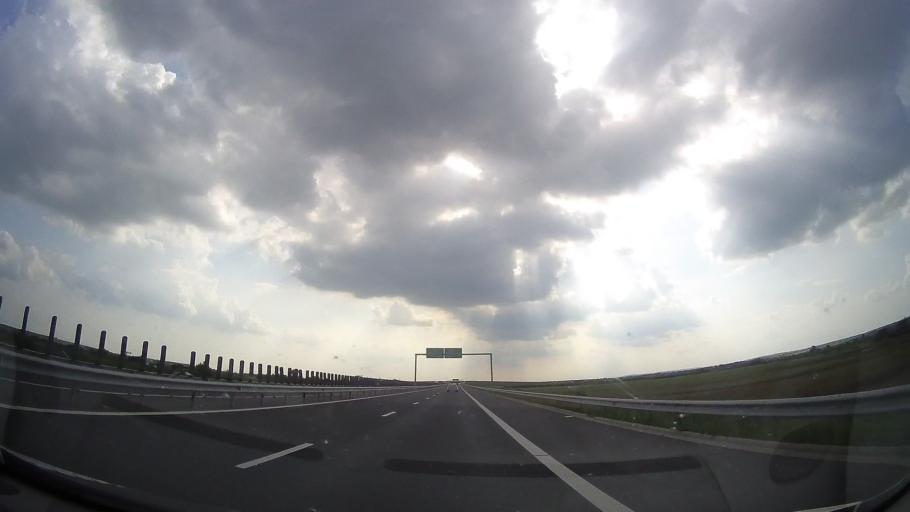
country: RO
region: Timis
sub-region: Comuna Balint
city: Balint
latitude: 45.8006
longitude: 21.8741
